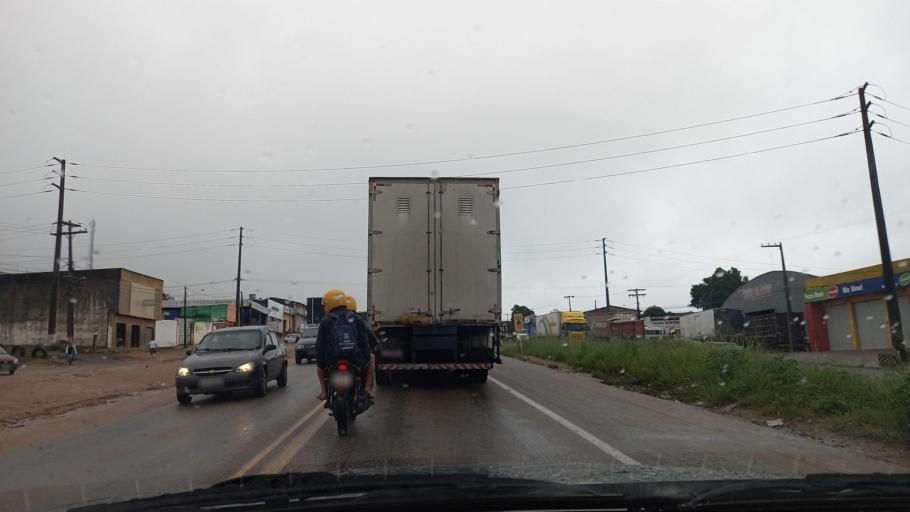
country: BR
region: Pernambuco
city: Garanhuns
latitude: -8.8811
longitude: -36.4916
